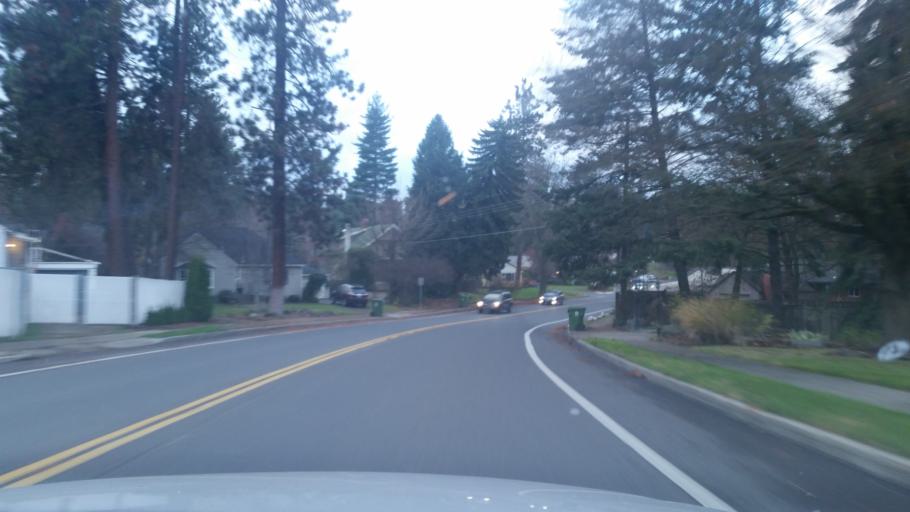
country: US
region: Washington
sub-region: Spokane County
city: Spokane
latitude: 47.6390
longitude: -117.3915
